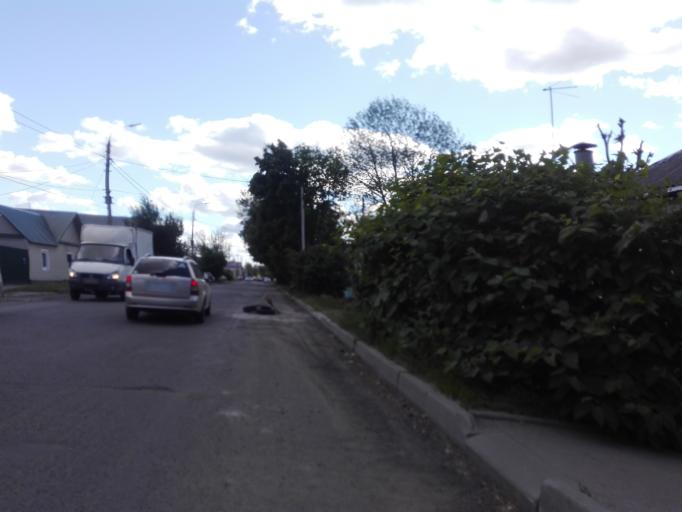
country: RU
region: Orjol
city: Orel
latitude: 52.9586
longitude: 36.0571
